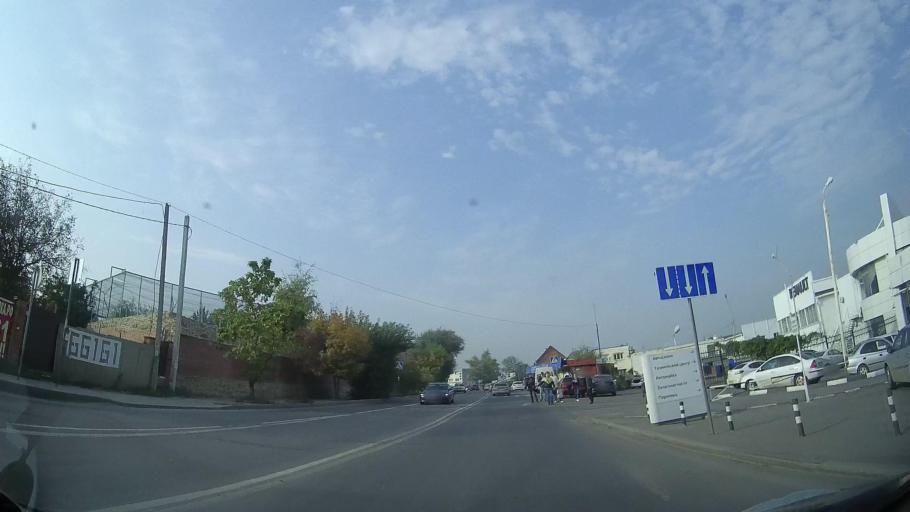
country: RU
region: Rostov
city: Severnyy
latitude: 47.2821
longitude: 39.6826
